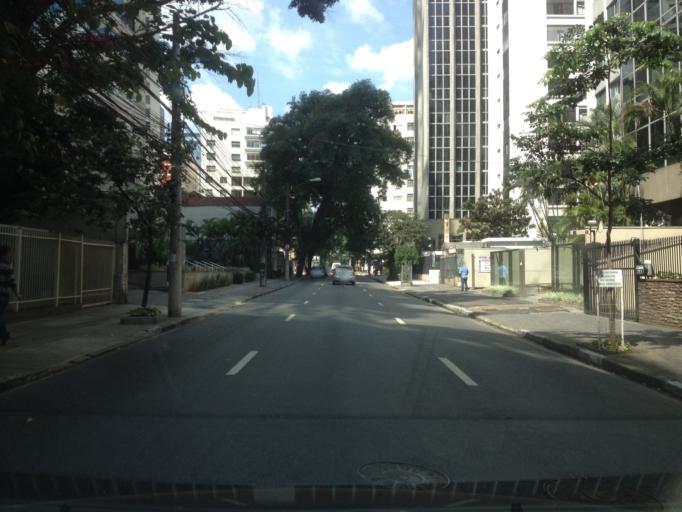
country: BR
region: Sao Paulo
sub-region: Sao Paulo
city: Sao Paulo
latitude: -23.5678
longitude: -46.6508
